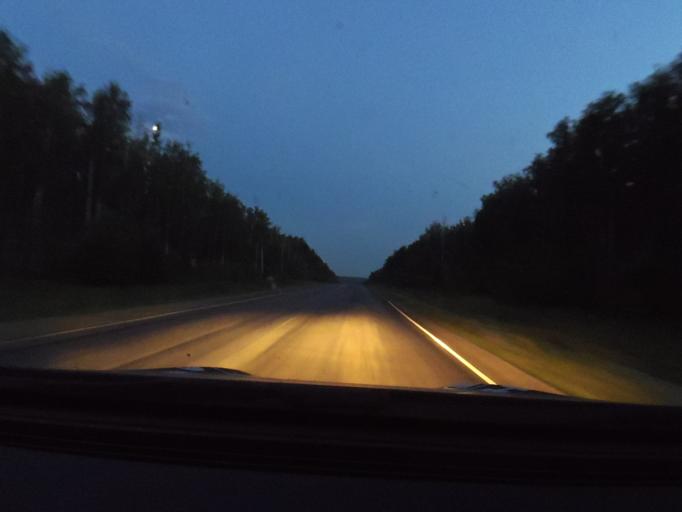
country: RU
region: Bashkortostan
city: Duvan
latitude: 55.9833
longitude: 58.2117
